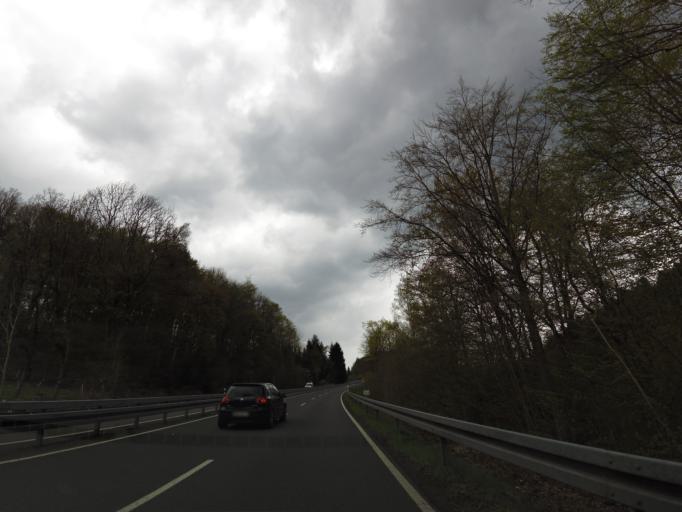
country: DE
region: Lower Saxony
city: Osterode am Harz
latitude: 51.7398
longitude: 10.2778
